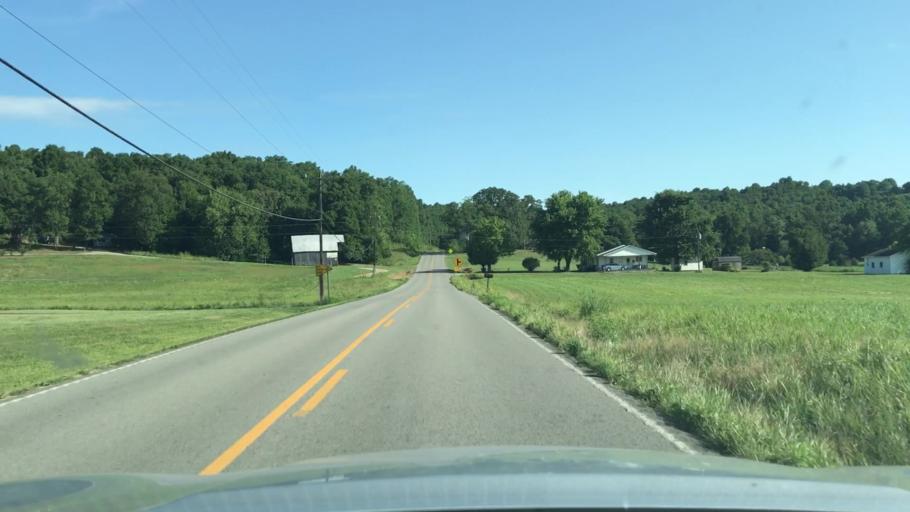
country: US
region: Kentucky
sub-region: Muhlenberg County
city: Greenville
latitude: 37.1060
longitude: -87.1273
